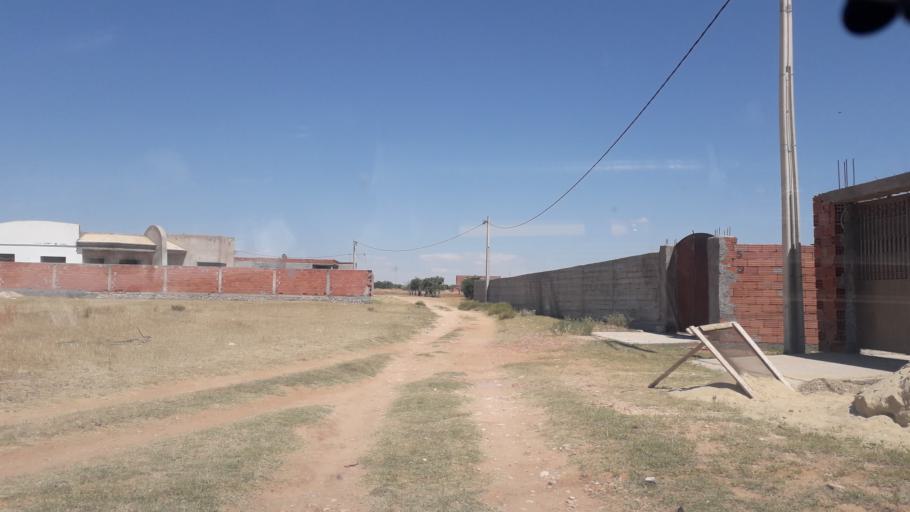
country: TN
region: Safaqis
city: Al Qarmadah
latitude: 34.8356
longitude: 10.7729
